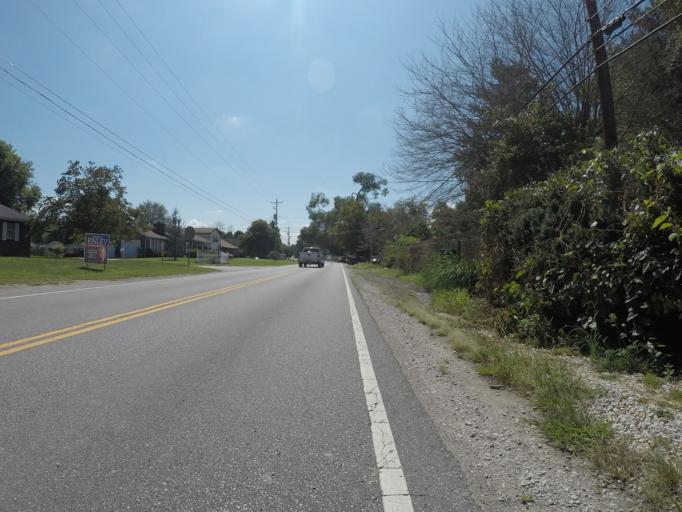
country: US
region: Ohio
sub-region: Lawrence County
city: South Point
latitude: 38.4563
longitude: -82.5965
